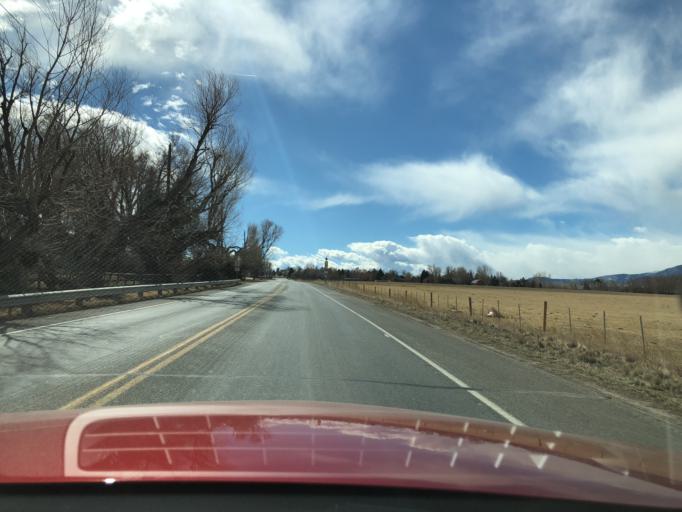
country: US
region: Colorado
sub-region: Boulder County
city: Superior
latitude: 40.0061
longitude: -105.1783
